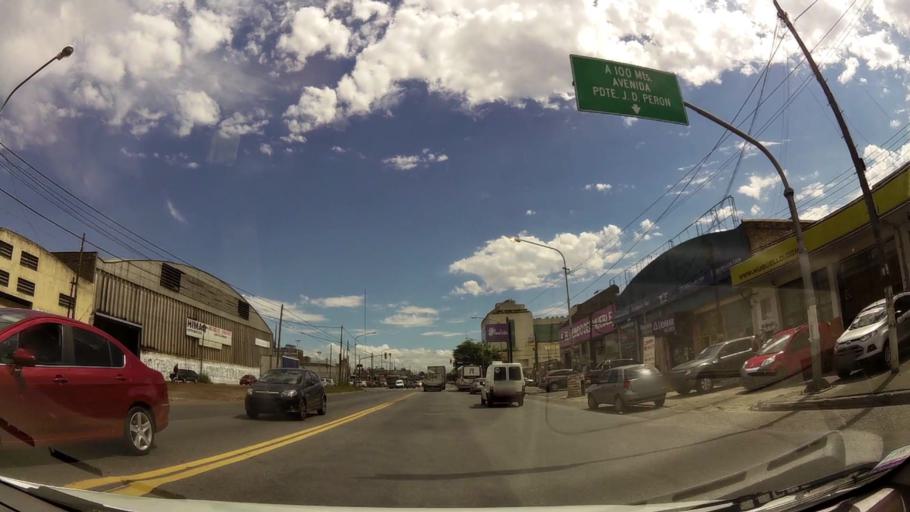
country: AR
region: Buenos Aires
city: San Justo
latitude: -34.6798
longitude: -58.5508
